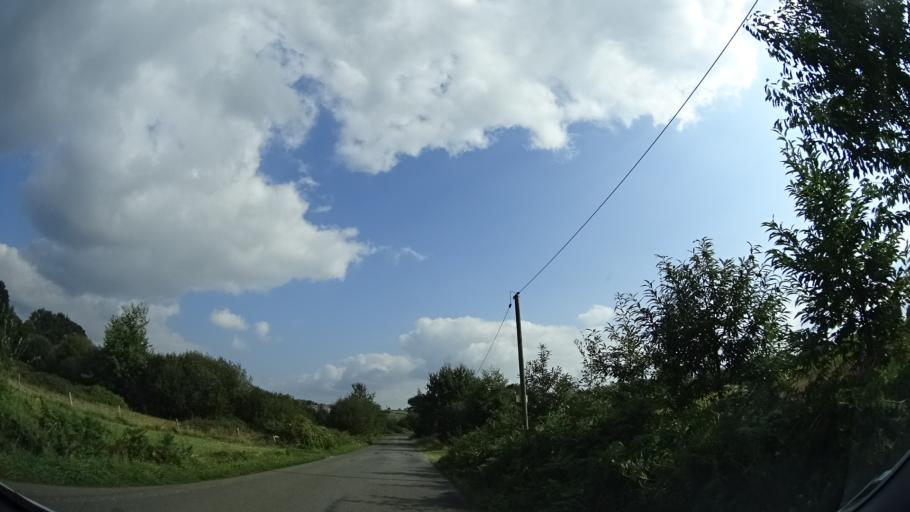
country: FR
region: Brittany
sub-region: Departement d'Ille-et-Vilaine
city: Pleumeleuc
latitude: 48.1977
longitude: -1.9070
